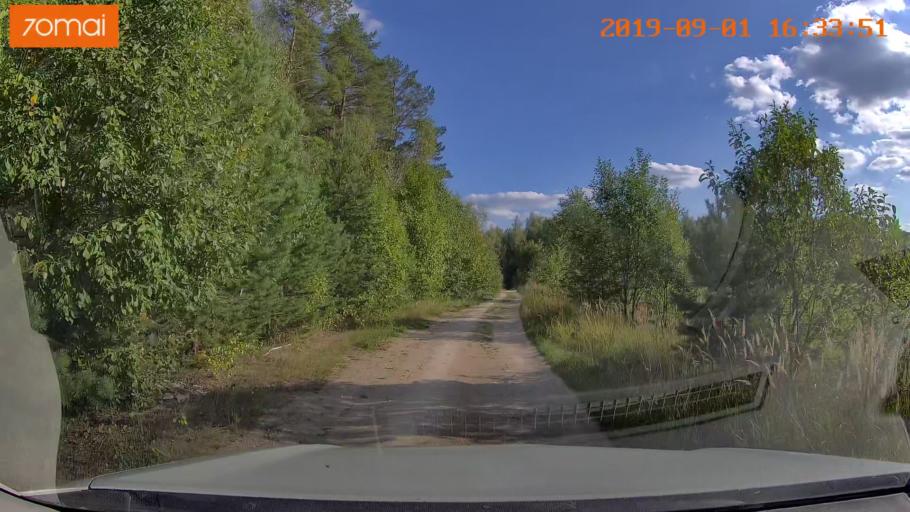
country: RU
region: Kaluga
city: Maloyaroslavets
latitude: 54.9493
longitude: 36.4748
